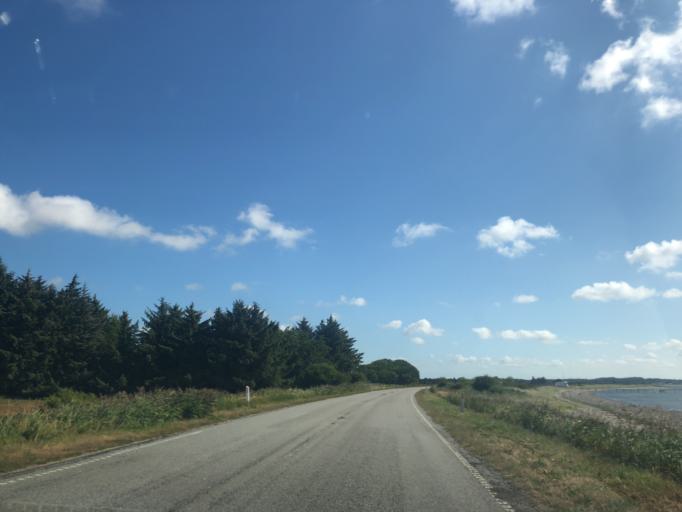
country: DK
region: North Denmark
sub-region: Morso Kommune
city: Nykobing Mors
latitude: 57.0161
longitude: 8.9803
